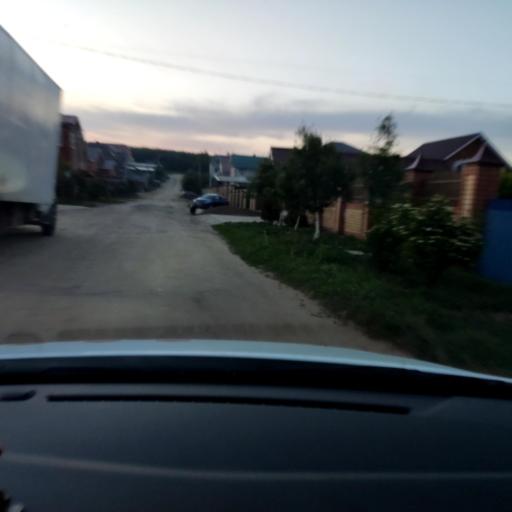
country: RU
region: Tatarstan
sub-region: Gorod Kazan'
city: Kazan
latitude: 55.8815
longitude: 49.1022
